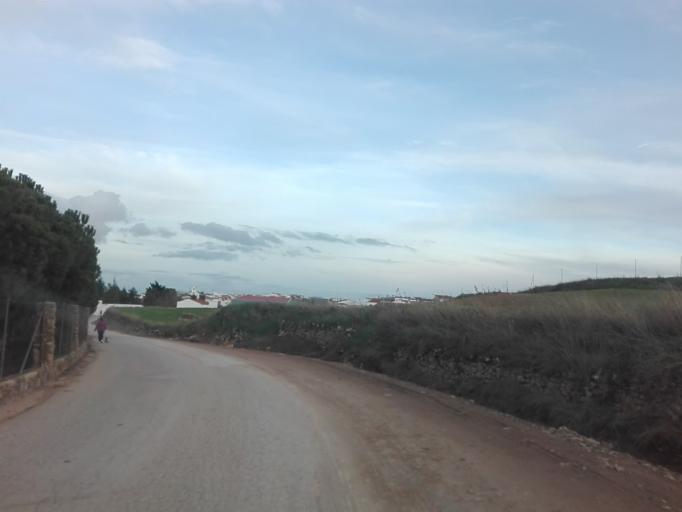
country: ES
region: Extremadura
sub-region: Provincia de Badajoz
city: Usagre
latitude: 38.3548
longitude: -6.1735
